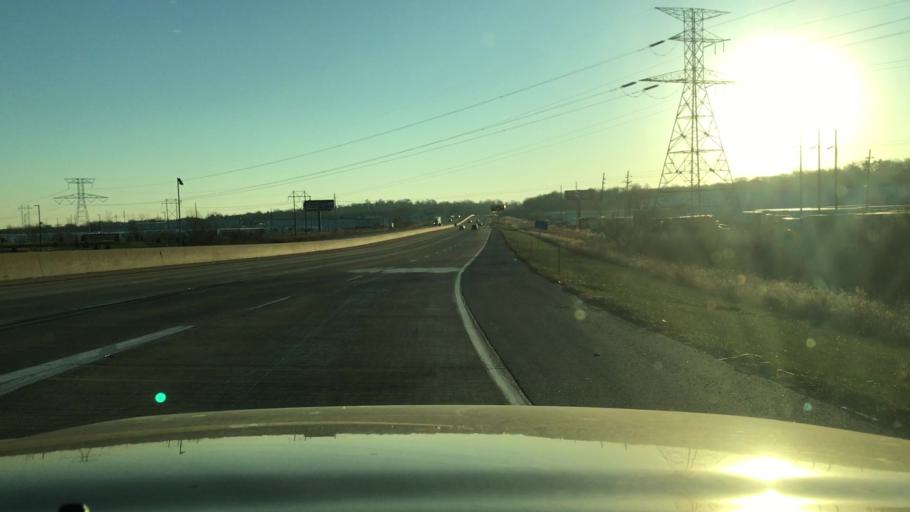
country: US
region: Missouri
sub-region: Saint Charles County
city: Saint Charles
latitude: 38.8232
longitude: -90.5150
